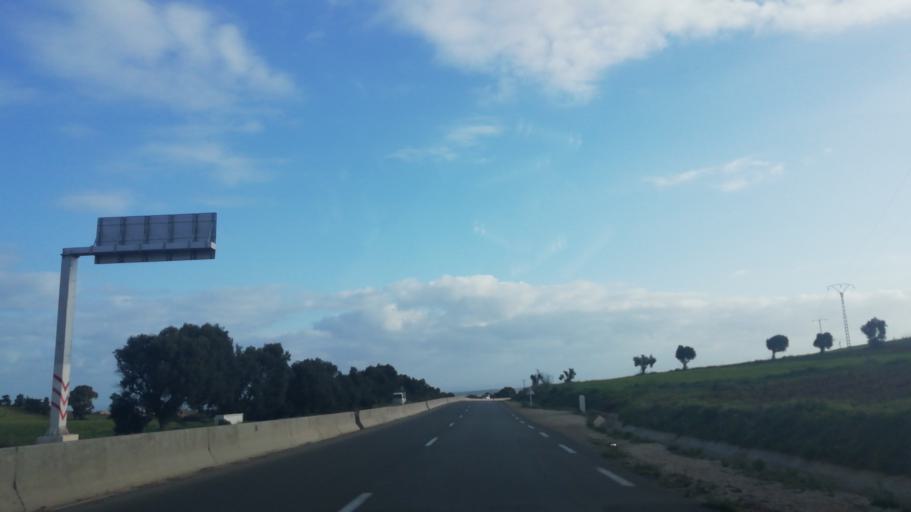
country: DZ
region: Mostaganem
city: Mostaganem
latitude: 36.1043
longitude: 0.2920
